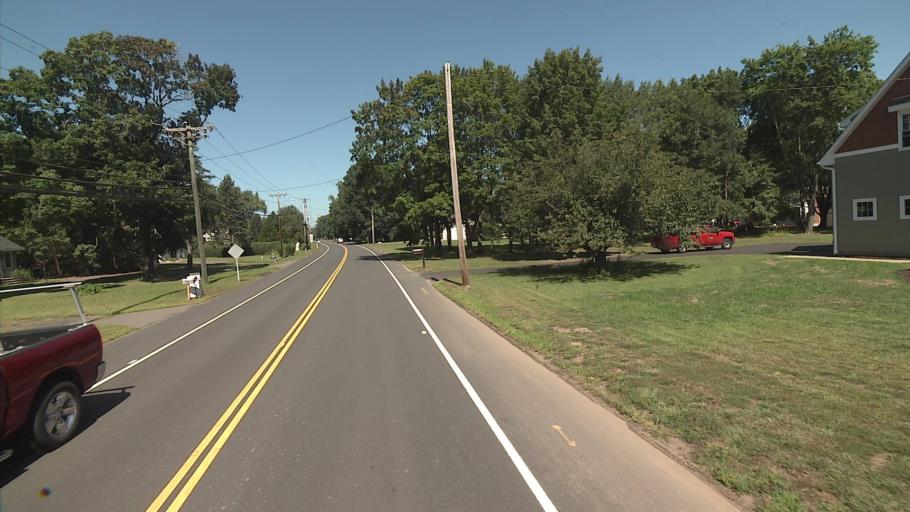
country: US
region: Connecticut
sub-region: Hartford County
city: Windsor
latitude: 41.8669
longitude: -72.6293
